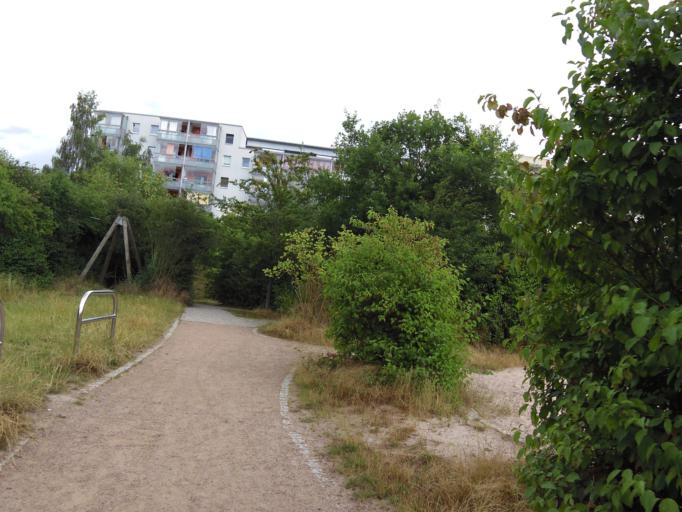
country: DE
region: Thuringia
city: Bad Salzungen
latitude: 50.8078
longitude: 10.2479
